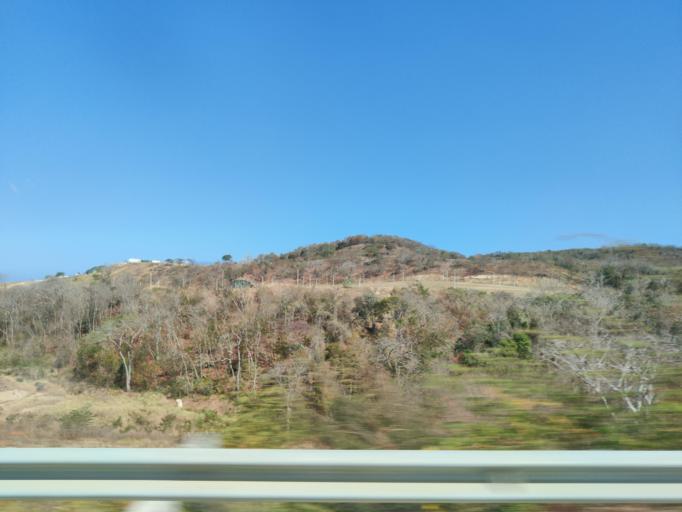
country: CO
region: Atlantico
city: Puerto Colombia
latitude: 10.9433
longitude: -75.0089
